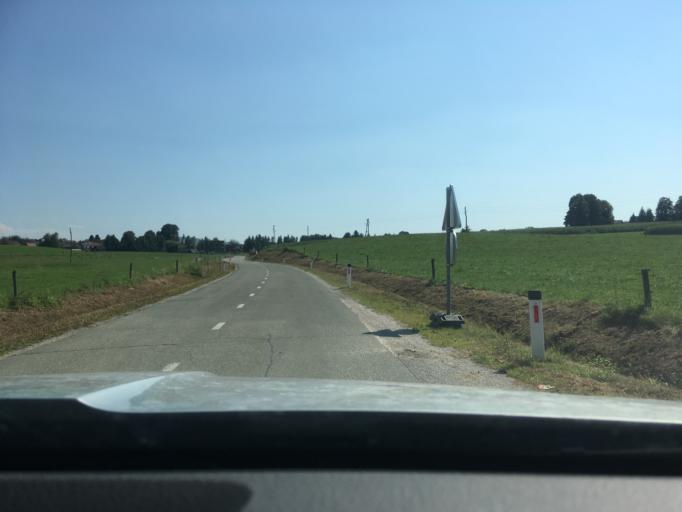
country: SI
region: Metlika
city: Metlika
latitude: 45.5952
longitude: 15.2772
